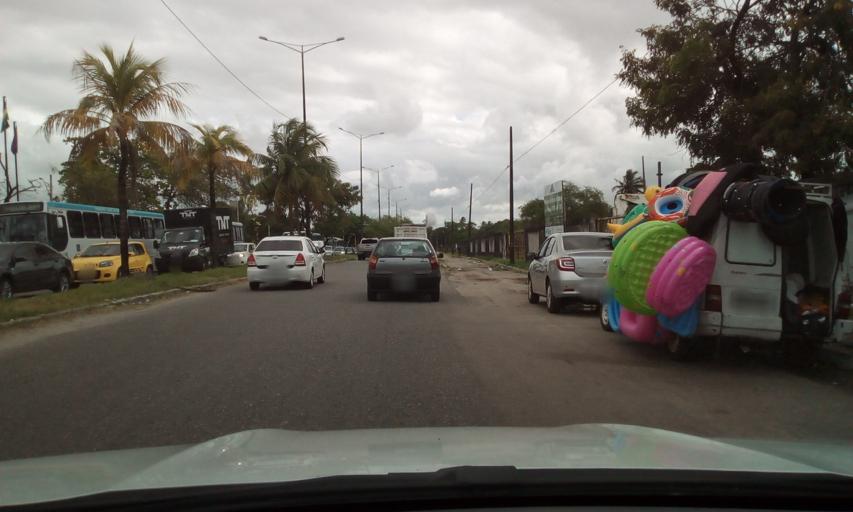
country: BR
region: Paraiba
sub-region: Joao Pessoa
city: Joao Pessoa
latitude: -7.1159
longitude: -34.8908
